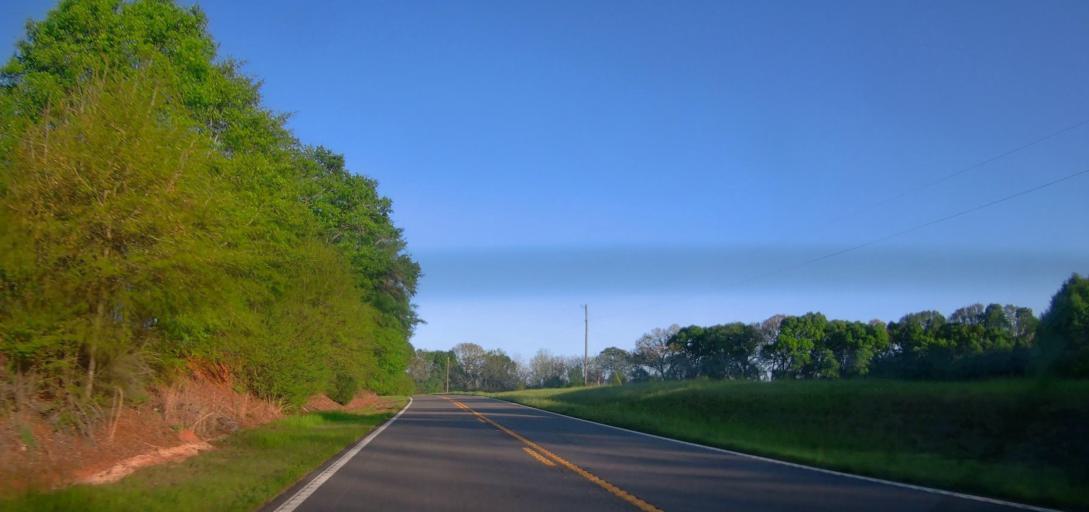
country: US
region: Georgia
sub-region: Marion County
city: Buena Vista
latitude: 32.3722
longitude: -84.4283
